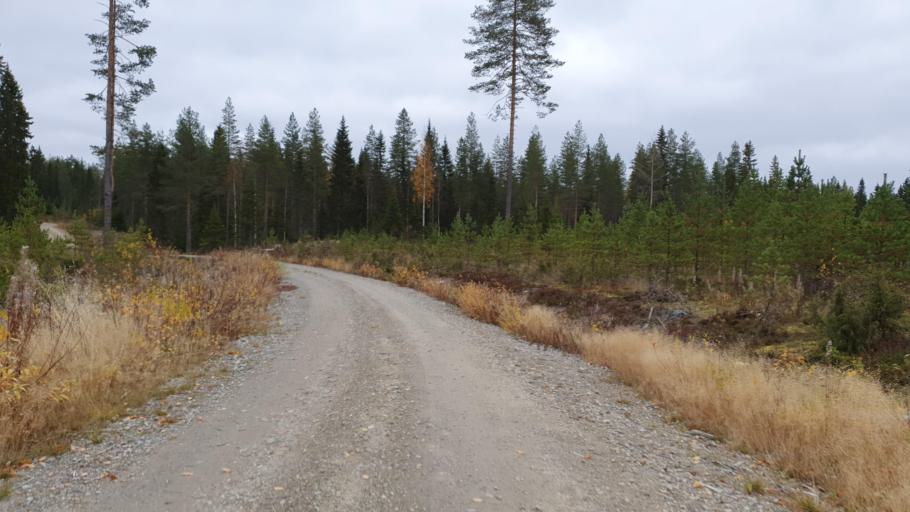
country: FI
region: Kainuu
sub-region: Kehys-Kainuu
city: Kuhmo
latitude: 64.4525
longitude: 29.6247
